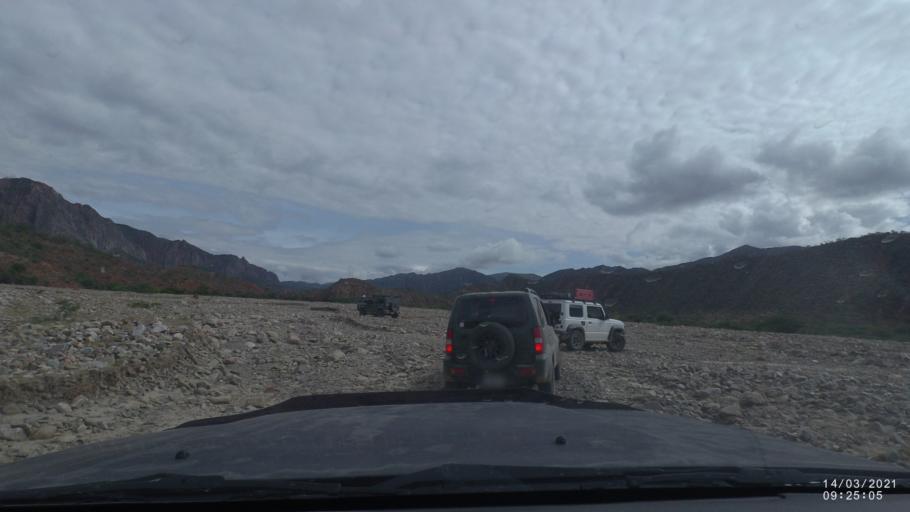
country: BO
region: Cochabamba
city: Cliza
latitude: -17.9484
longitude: -65.8560
